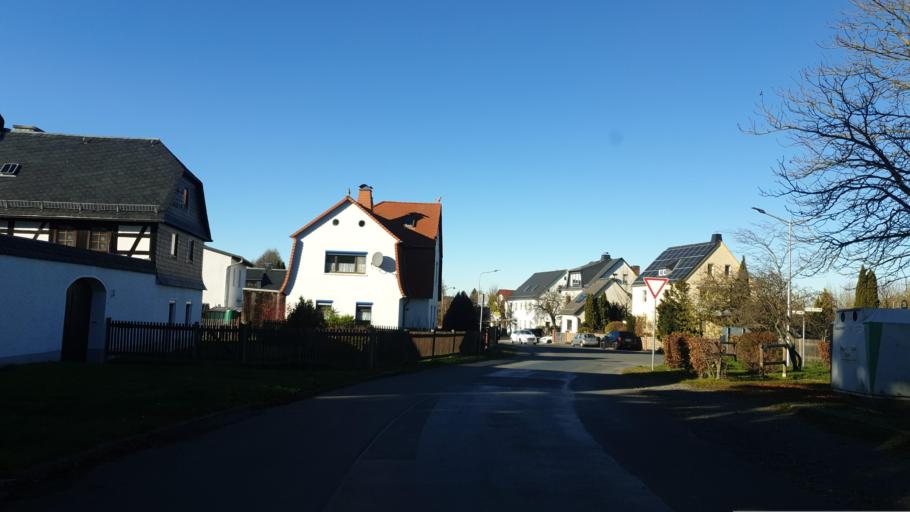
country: DE
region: Saxony
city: Elsterberg
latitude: 50.6387
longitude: 12.1529
